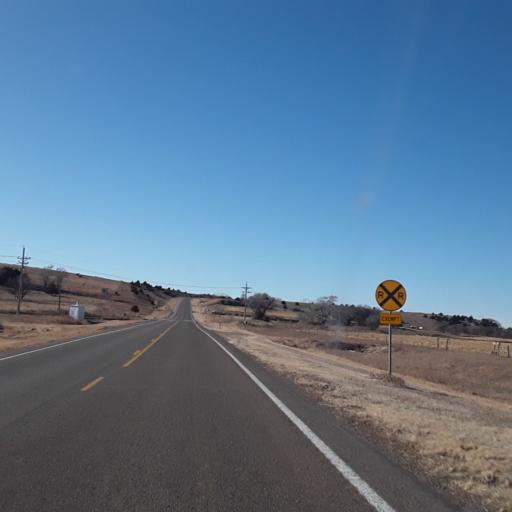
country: US
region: Nebraska
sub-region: Frontier County
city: Stockville
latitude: 40.6326
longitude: -100.5725
